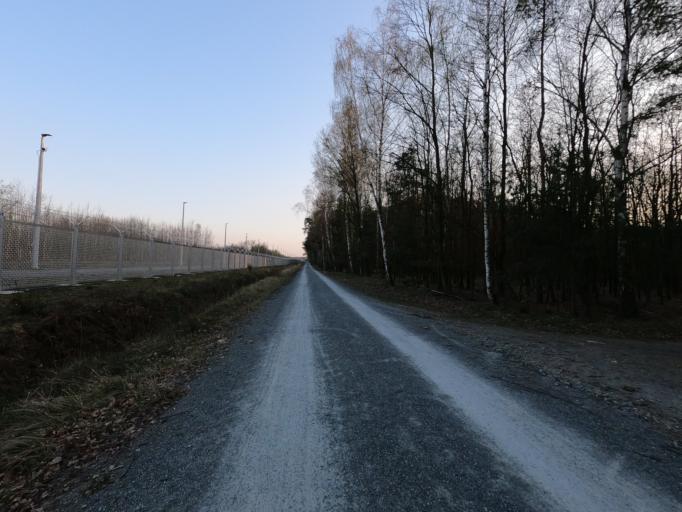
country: DE
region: Hesse
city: Kelsterbach
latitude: 50.0099
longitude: 8.5221
